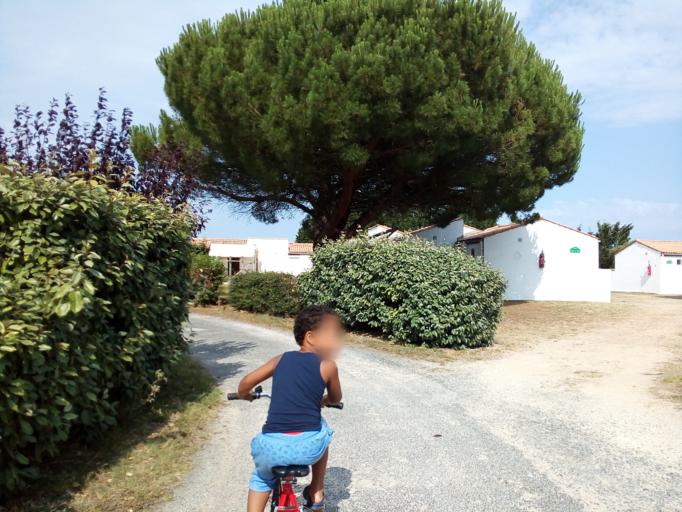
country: FR
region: Poitou-Charentes
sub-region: Departement de la Charente-Maritime
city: Boyard-Ville
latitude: 45.9510
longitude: -1.2440
